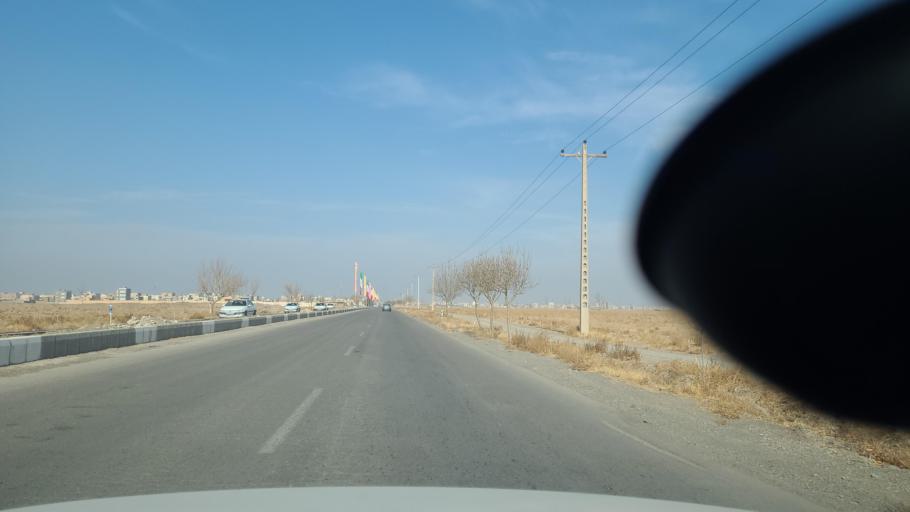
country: IR
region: Razavi Khorasan
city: Fariman
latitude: 35.6750
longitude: 59.8425
